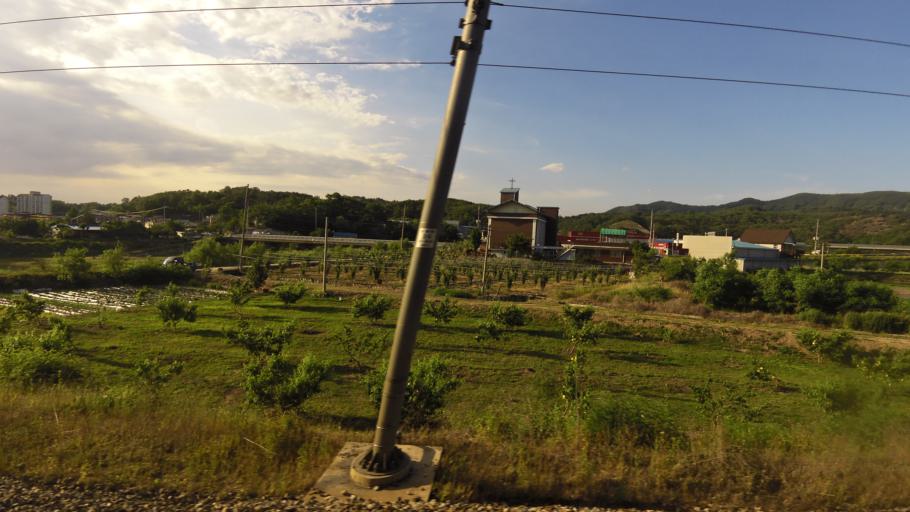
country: KR
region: Chungcheongbuk-do
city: Yong-dong
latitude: 36.1703
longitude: 127.7933
